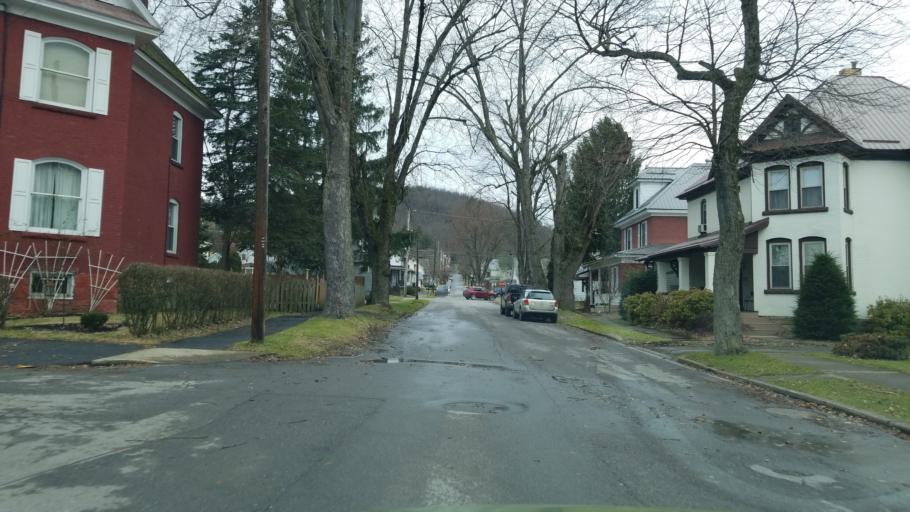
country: US
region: Pennsylvania
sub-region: Clearfield County
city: Clearfield
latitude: 41.0257
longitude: -78.4450
